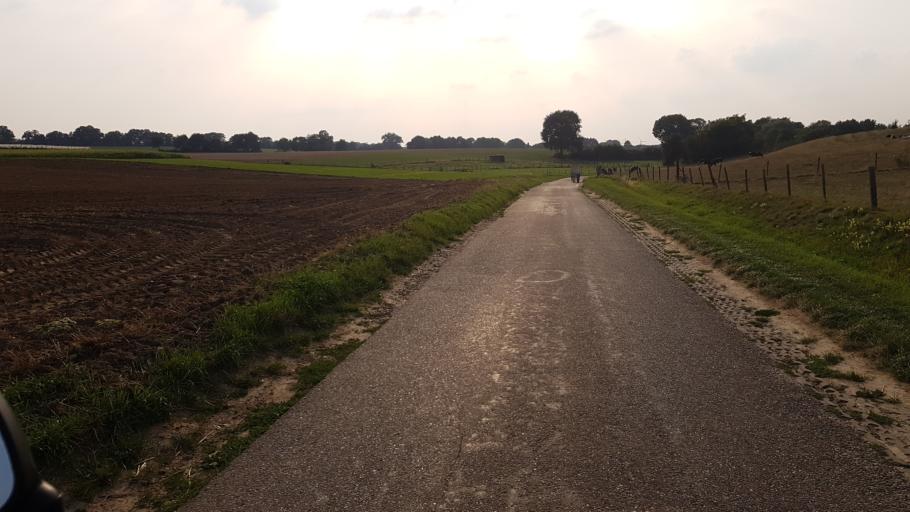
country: NL
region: Limburg
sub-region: Gemeente Stein
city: Elsloo
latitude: 50.9370
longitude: 5.7797
